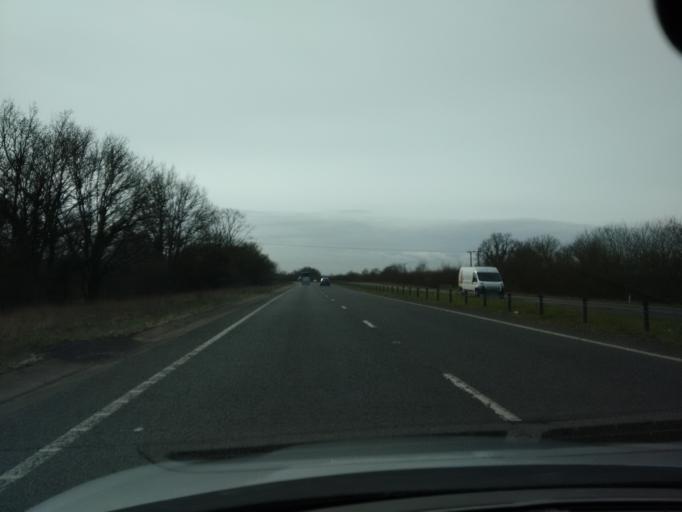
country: GB
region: England
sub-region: Warwickshire
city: Bidford-on-avon
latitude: 52.1728
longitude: -1.8825
